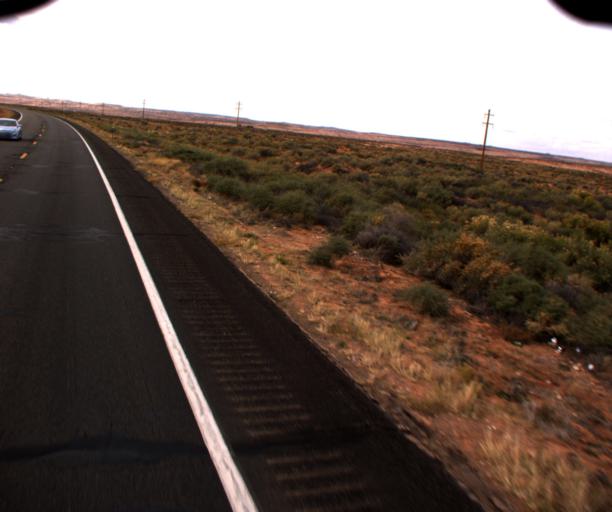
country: US
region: Arizona
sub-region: Apache County
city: Many Farms
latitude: 36.9415
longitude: -109.6477
